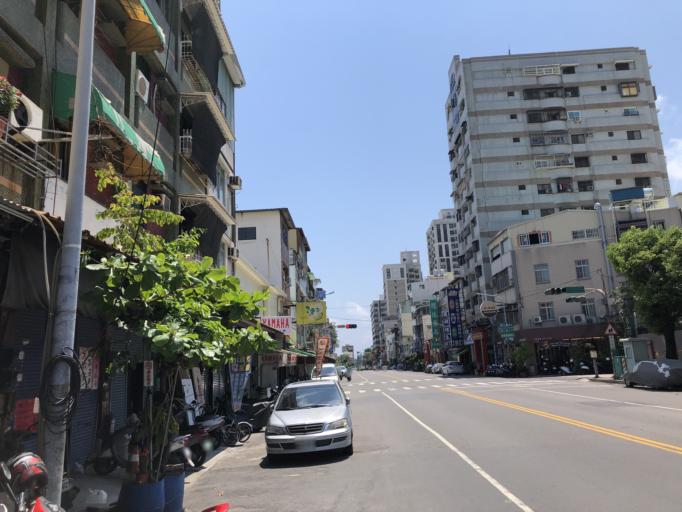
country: TW
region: Kaohsiung
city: Kaohsiung
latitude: 22.6312
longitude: 120.2815
